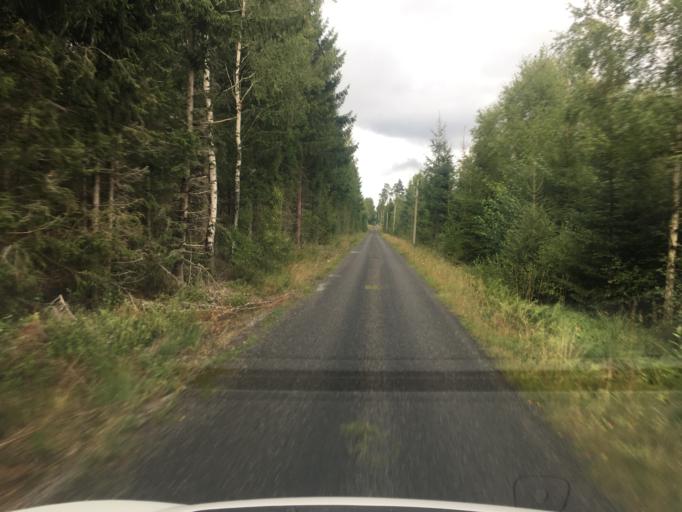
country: SE
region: Kronoberg
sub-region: Ljungby Kommun
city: Lagan
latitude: 56.9416
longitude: 14.0286
